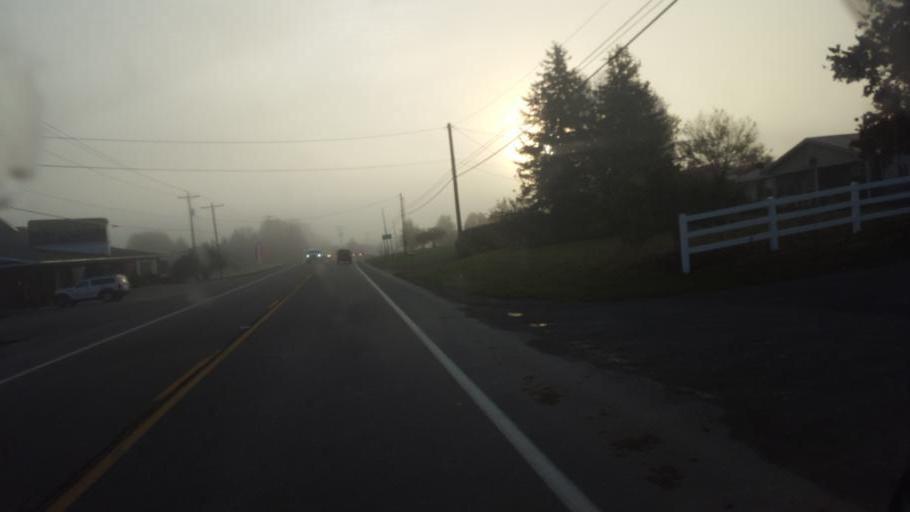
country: US
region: Ohio
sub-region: Tuscarawas County
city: Sugarcreek
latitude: 40.5464
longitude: -81.7466
